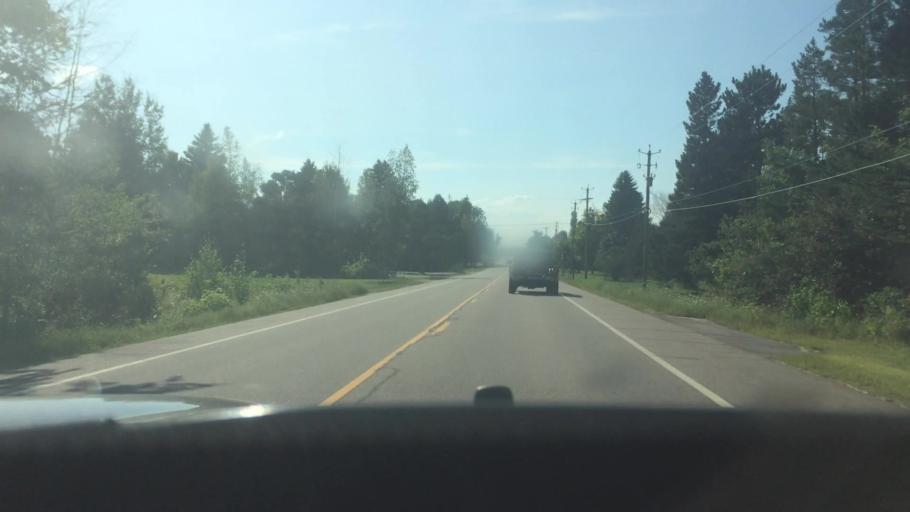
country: US
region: New York
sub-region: Franklin County
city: Malone
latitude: 44.8584
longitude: -74.2378
